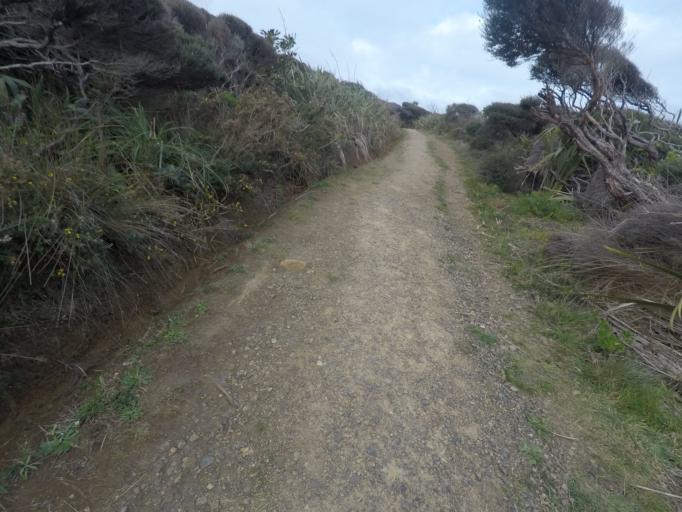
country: NZ
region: Auckland
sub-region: Auckland
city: Muriwai Beach
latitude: -36.9740
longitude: 174.4721
